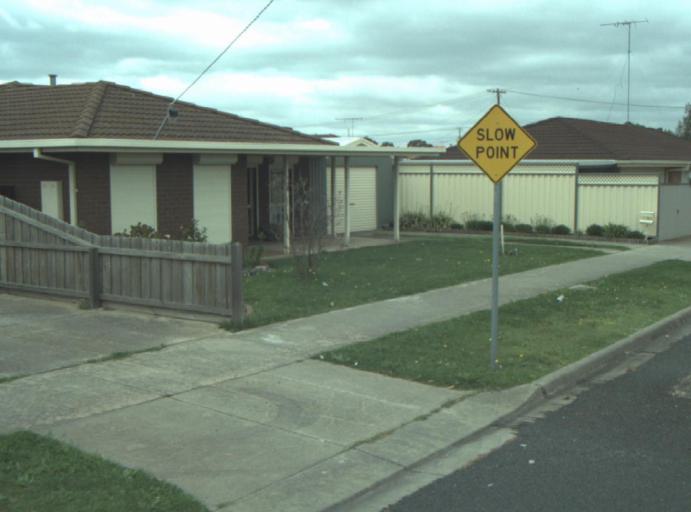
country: AU
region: Victoria
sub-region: Greater Geelong
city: Bell Post Hill
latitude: -38.0710
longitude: 144.3441
